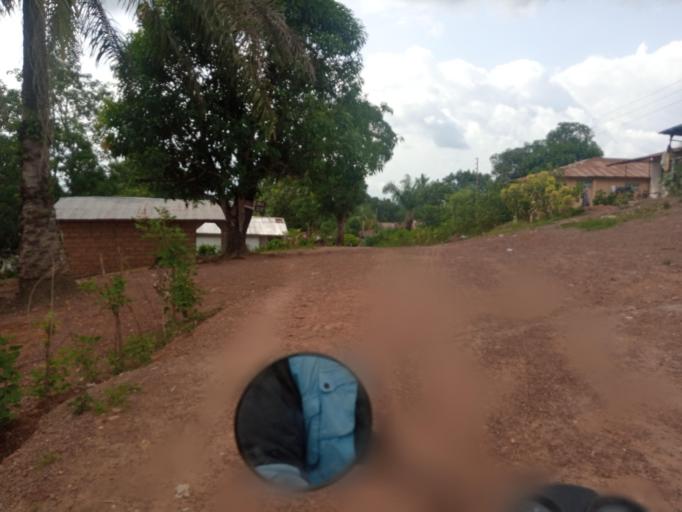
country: SL
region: Southern Province
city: Bo
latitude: 7.9851
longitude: -11.7425
